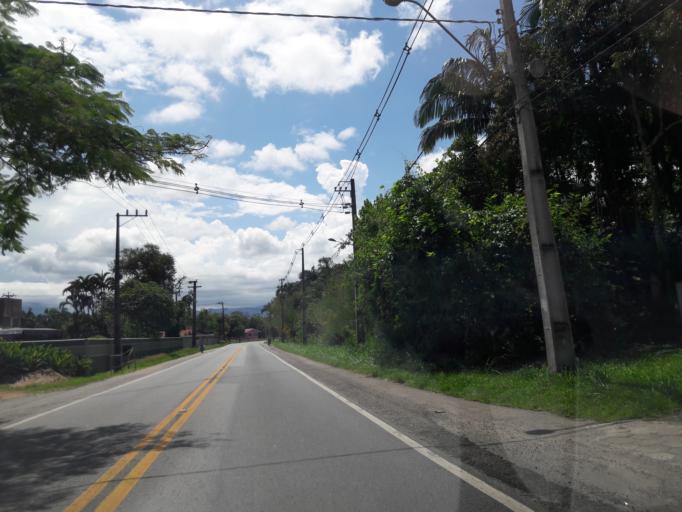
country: BR
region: Parana
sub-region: Antonina
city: Antonina
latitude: -25.4721
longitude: -48.8292
